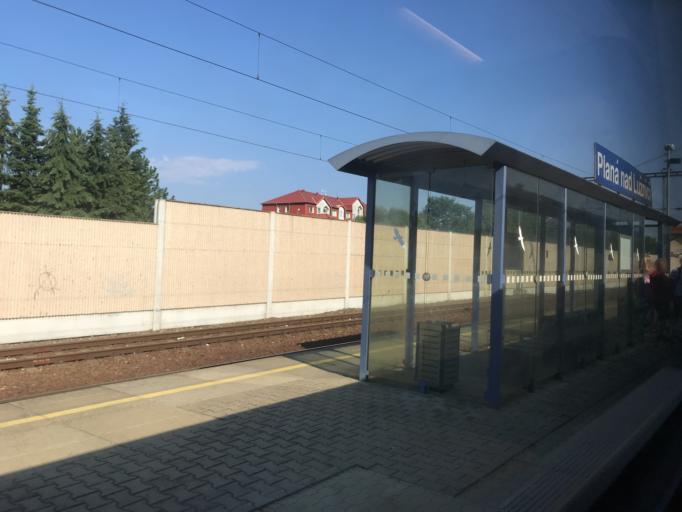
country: CZ
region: Jihocesky
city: Plana nad Luznici
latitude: 49.3522
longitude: 14.7070
